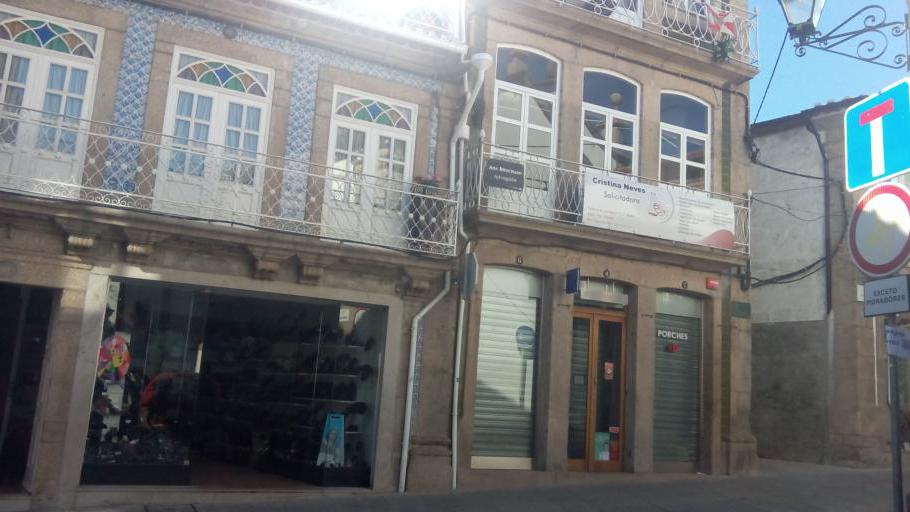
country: PT
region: Porto
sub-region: Penafiel
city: Penafiel
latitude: 41.2065
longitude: -8.2834
